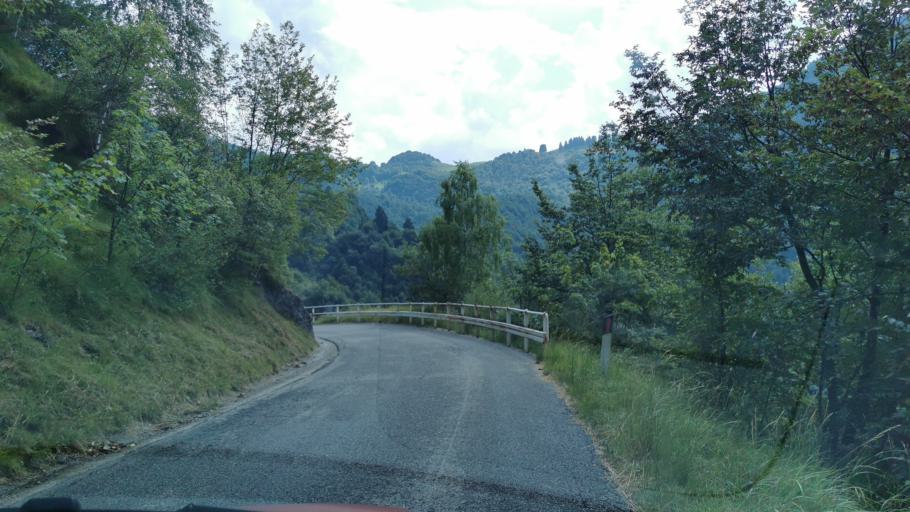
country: IT
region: Lombardy
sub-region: Provincia di Lecco
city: Moggio
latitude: 45.9171
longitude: 9.4912
